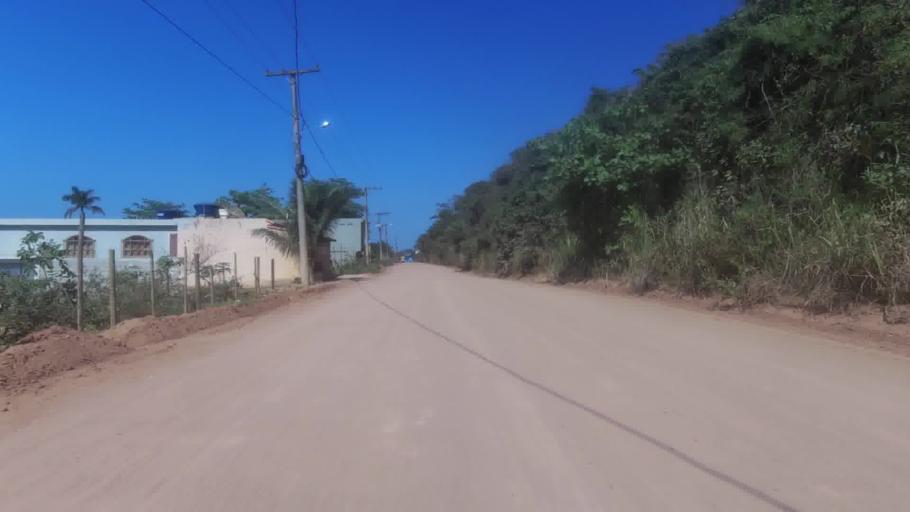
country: BR
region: Espirito Santo
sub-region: Marataizes
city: Marataizes
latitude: -21.0851
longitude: -40.8438
